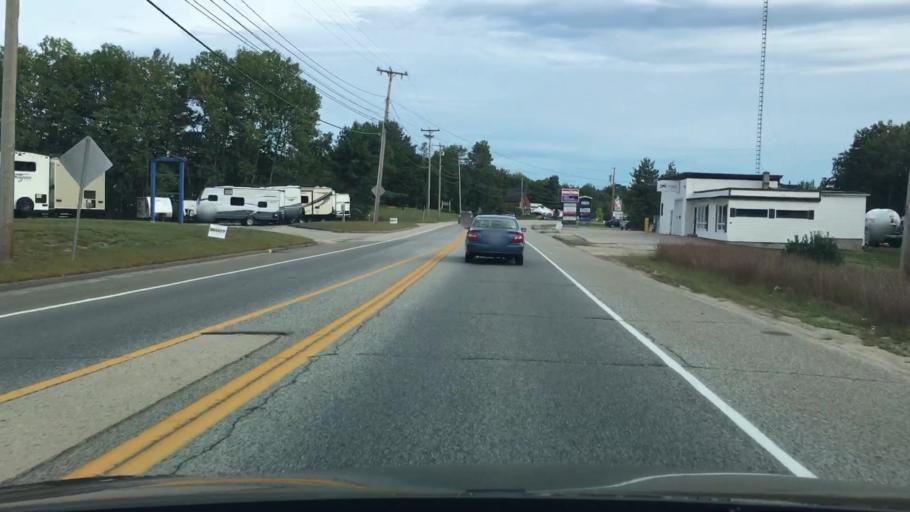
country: US
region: Maine
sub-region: Cumberland County
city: Bridgton
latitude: 44.0433
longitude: -70.7006
